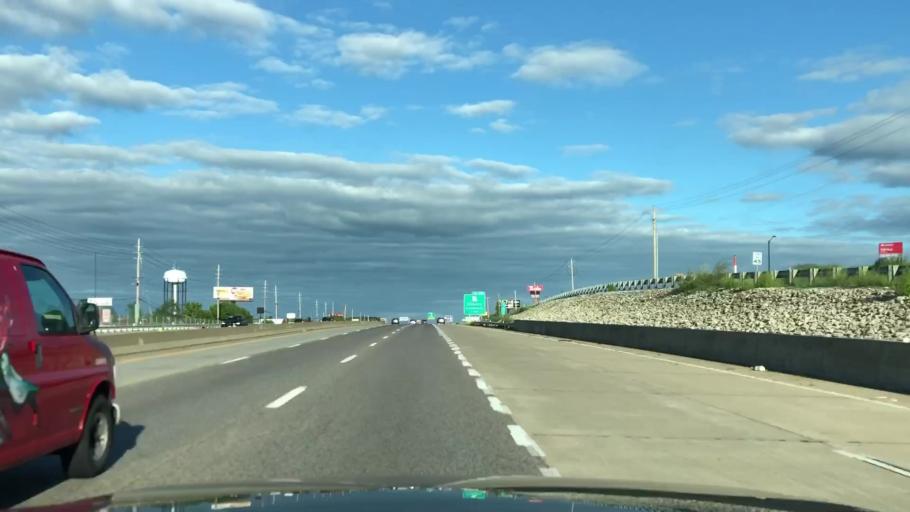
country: US
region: Missouri
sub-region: Saint Charles County
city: O'Fallon
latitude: 38.8025
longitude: -90.6721
